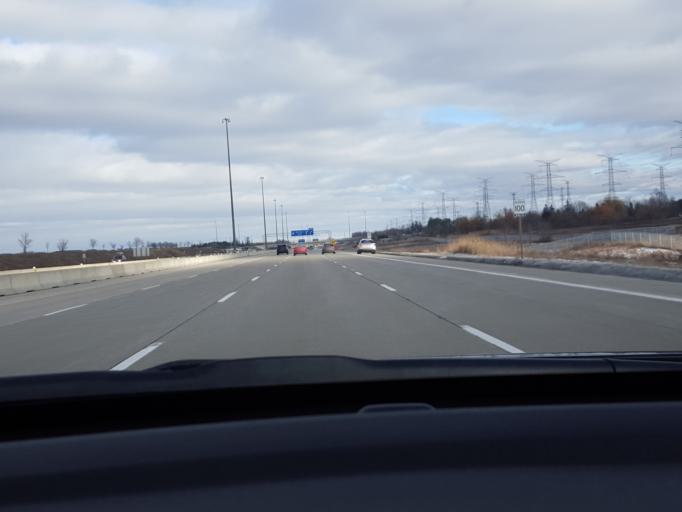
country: CA
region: Ontario
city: Markham
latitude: 43.8528
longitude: -79.2959
